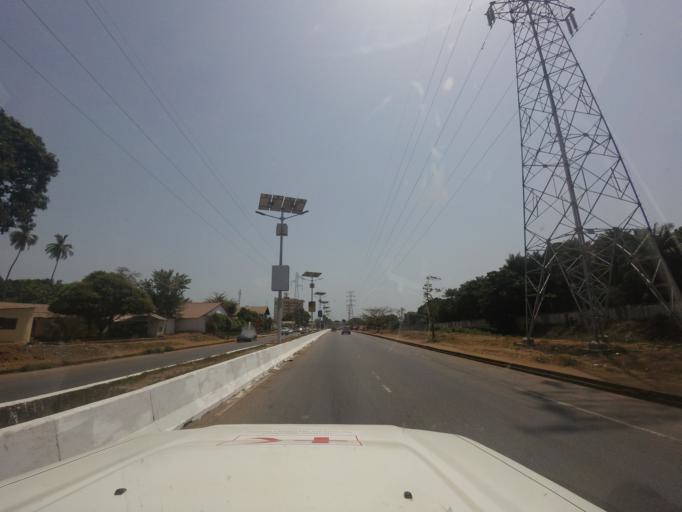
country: GN
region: Conakry
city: Camayenne
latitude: 9.5288
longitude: -13.6855
